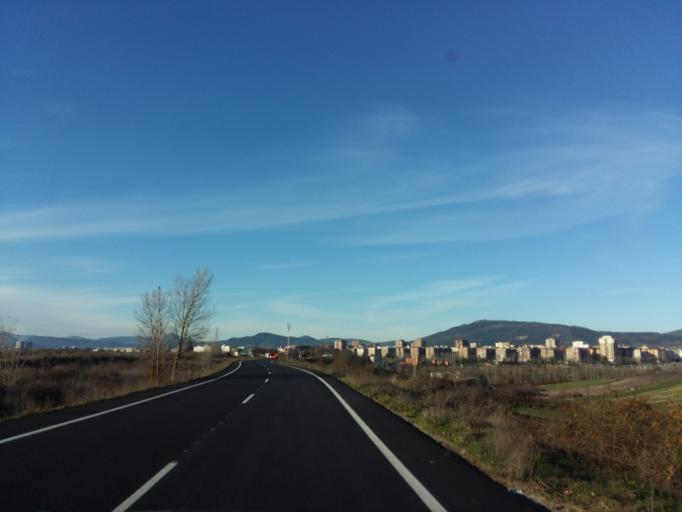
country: ES
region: Navarre
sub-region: Provincia de Navarra
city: Iturrama
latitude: 42.7922
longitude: -1.6501
